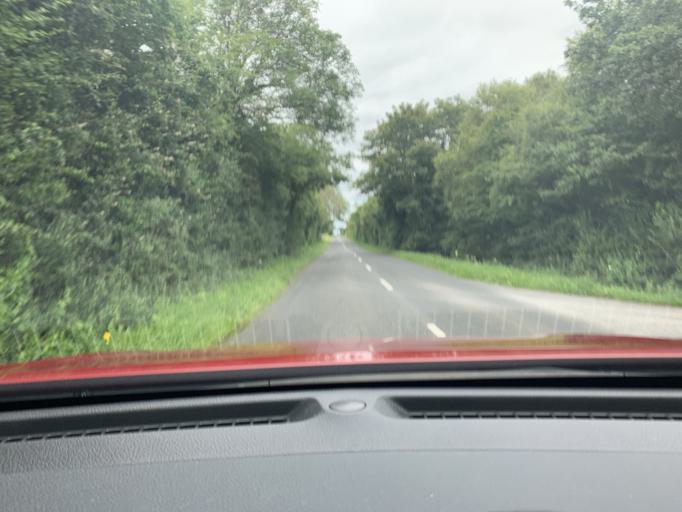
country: GB
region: Northern Ireland
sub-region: Fermanagh District
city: Enniskillen
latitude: 54.2879
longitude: -7.6987
